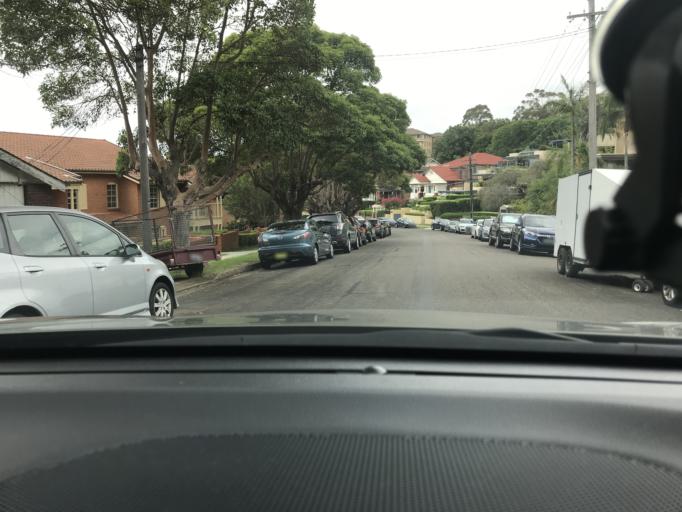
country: AU
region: New South Wales
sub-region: Hunters Hill
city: Gladesville
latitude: -33.8445
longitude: 151.1293
